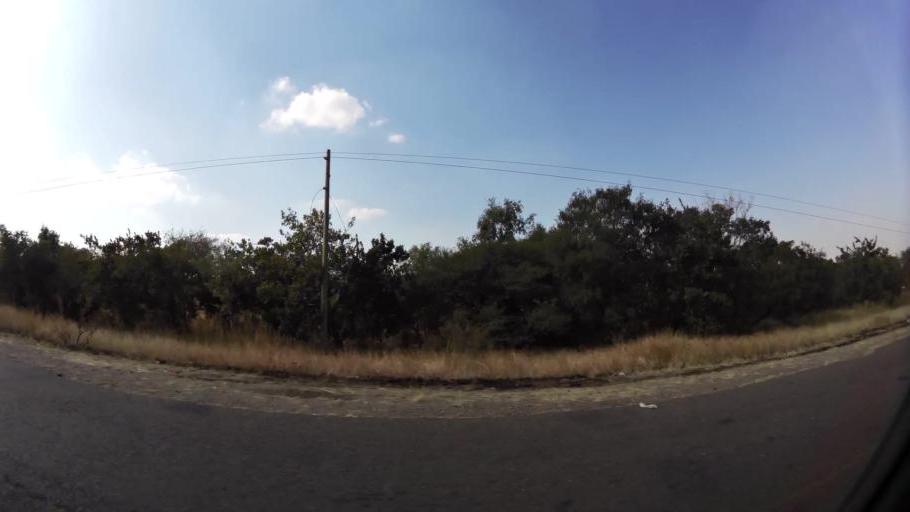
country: ZA
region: North-West
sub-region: Bojanala Platinum District Municipality
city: Rustenburg
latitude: -25.6341
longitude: 27.1940
